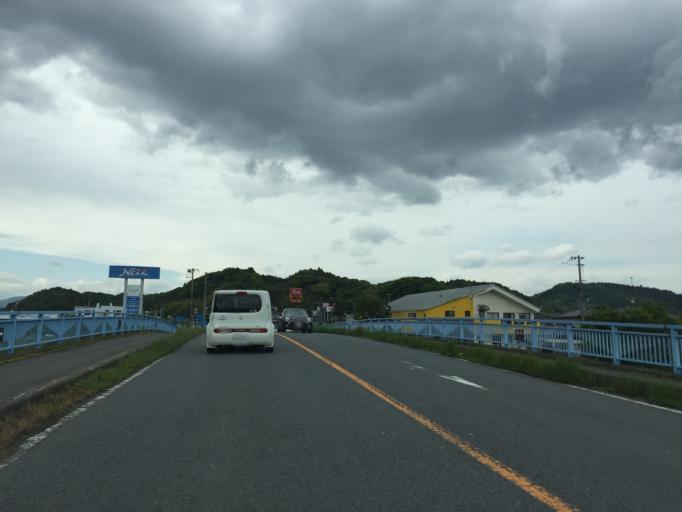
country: JP
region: Fukushima
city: Iwaki
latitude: 36.9843
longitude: 140.8698
